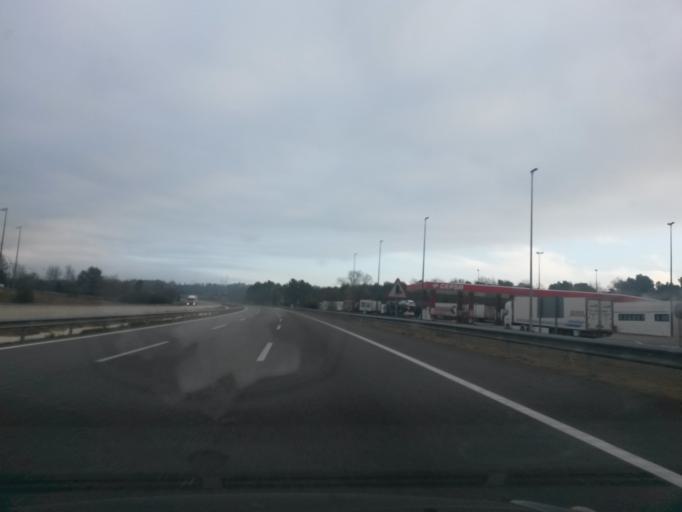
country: ES
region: Catalonia
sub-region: Provincia de Girona
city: Pontos
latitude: 42.1732
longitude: 2.9308
